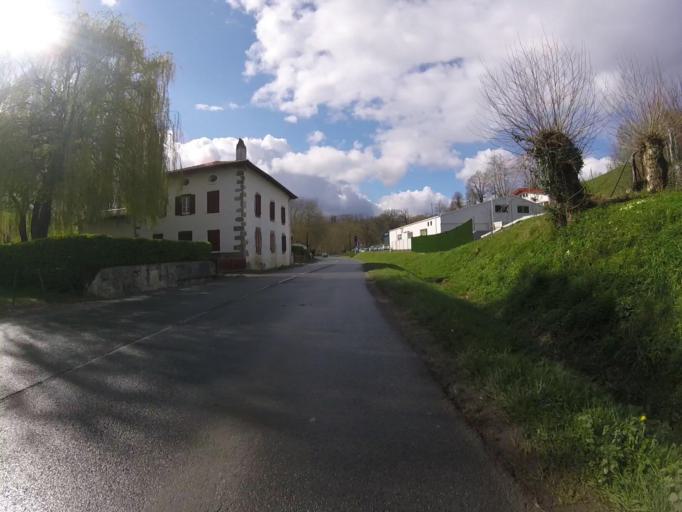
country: FR
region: Aquitaine
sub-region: Departement des Pyrenees-Atlantiques
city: Sare
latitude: 43.3051
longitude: -1.5728
